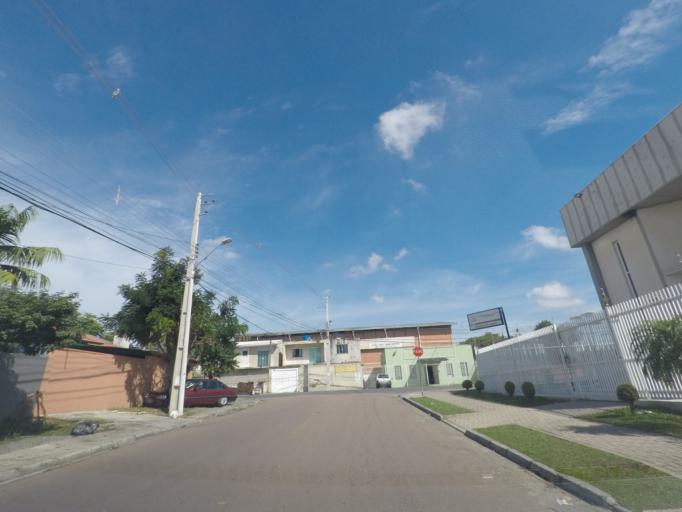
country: BR
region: Parana
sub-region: Curitiba
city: Curitiba
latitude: -25.4691
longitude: -49.2651
